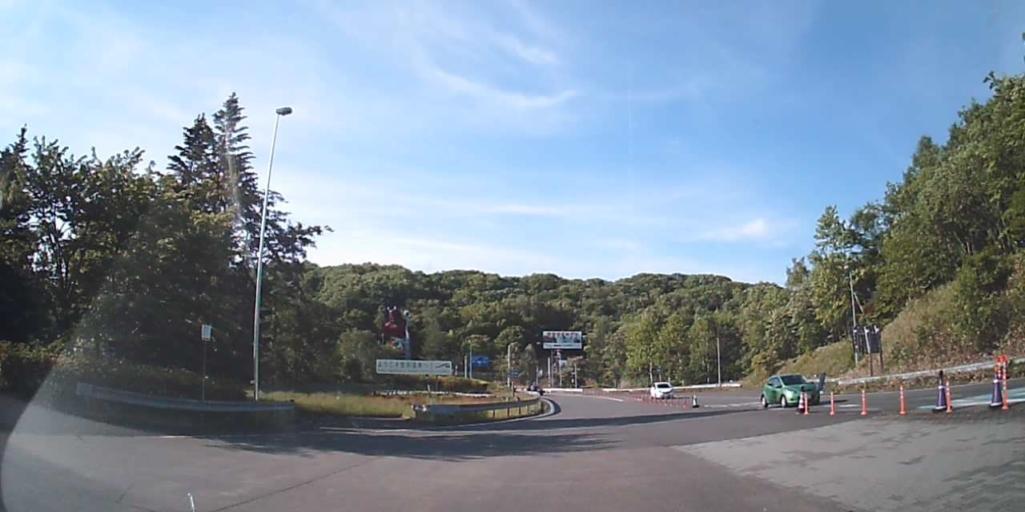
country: JP
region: Hokkaido
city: Shiraoi
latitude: 42.4640
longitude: 141.1736
